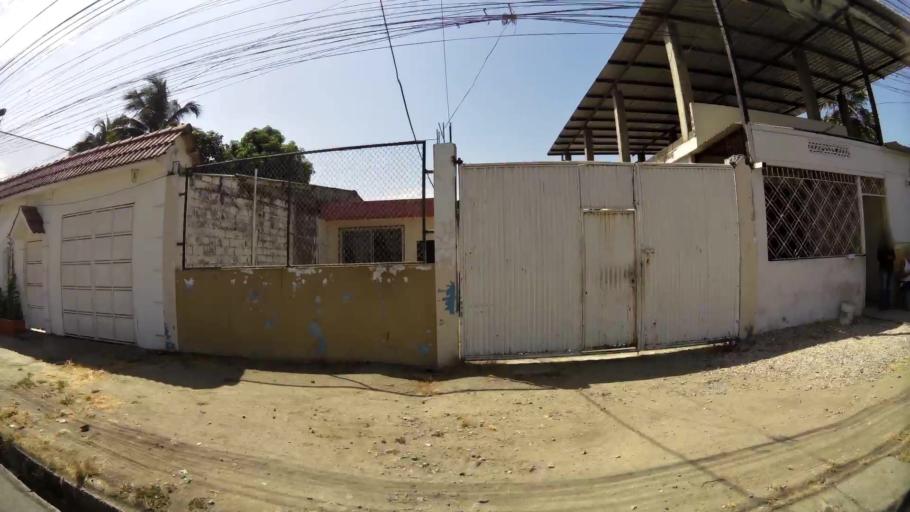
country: EC
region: Guayas
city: Eloy Alfaro
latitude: -2.1275
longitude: -79.9139
